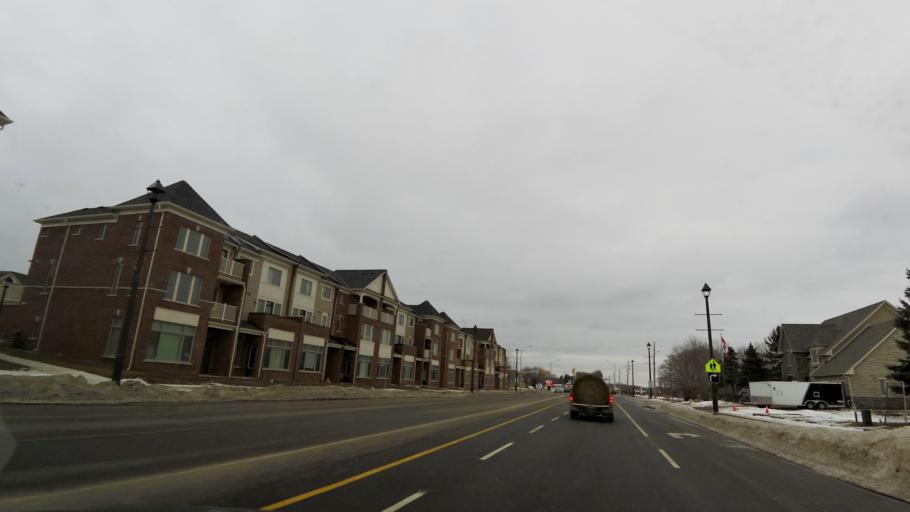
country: CA
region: Ontario
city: Brampton
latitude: 43.8777
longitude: -79.8562
